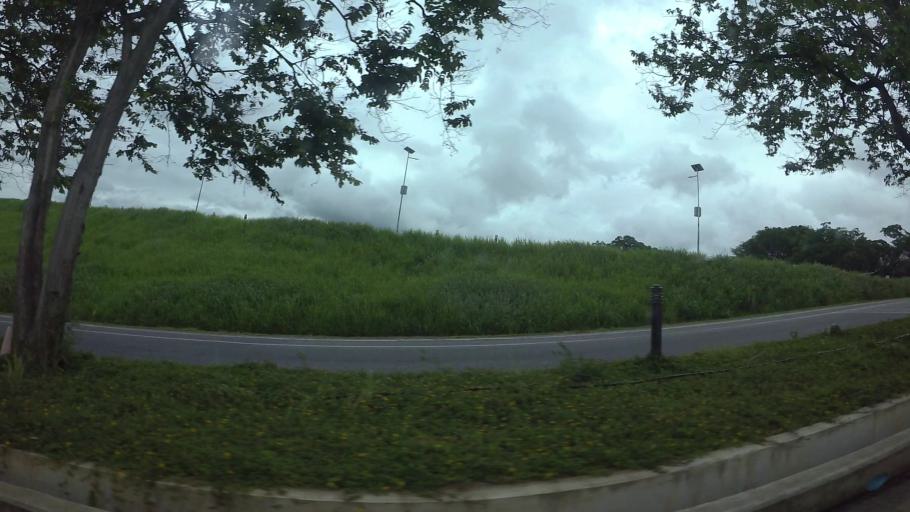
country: TH
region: Chon Buri
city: Si Racha
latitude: 13.2085
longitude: 100.9610
